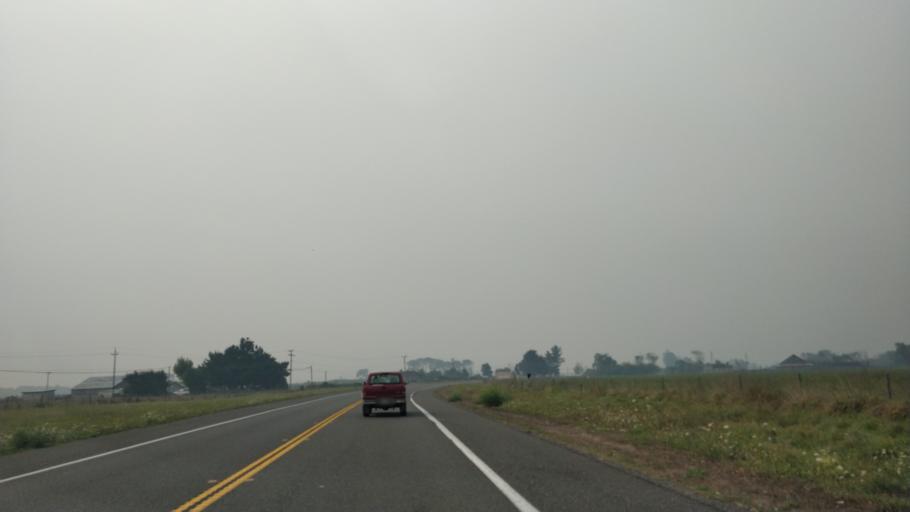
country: US
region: California
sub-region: Humboldt County
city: Ferndale
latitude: 40.5968
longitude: -124.2335
